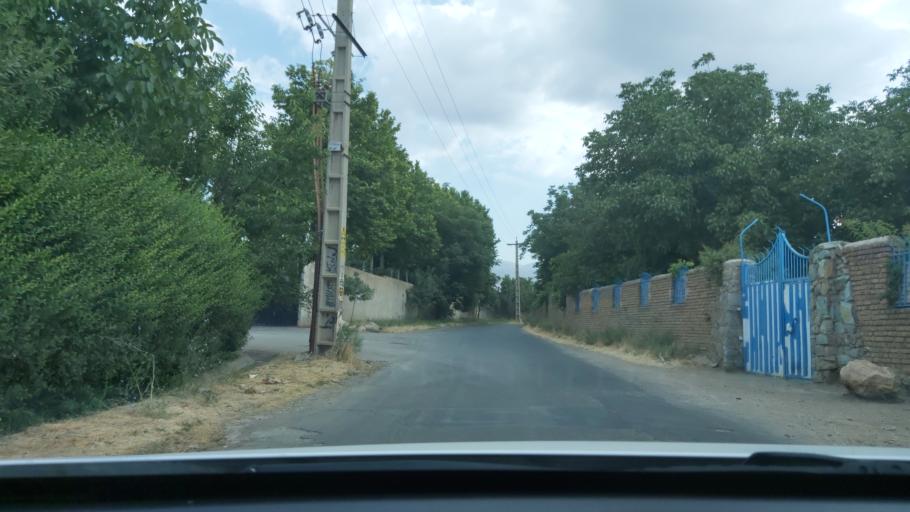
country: IR
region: Alborz
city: Hashtgerd
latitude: 35.9500
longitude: 50.7739
